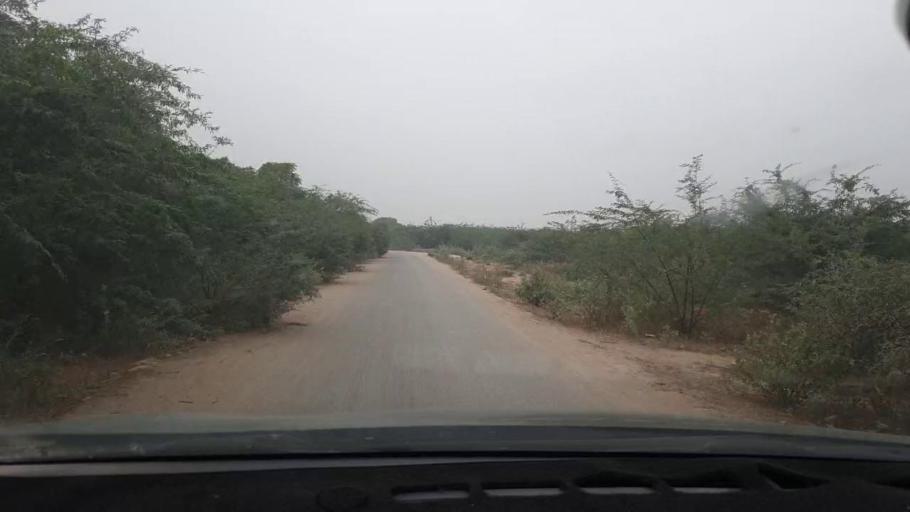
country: PK
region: Sindh
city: Malir Cantonment
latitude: 24.9258
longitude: 67.3222
